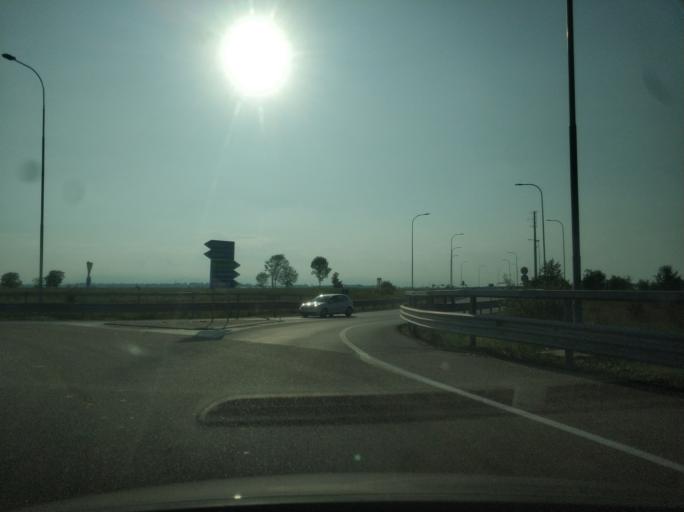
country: IT
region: Piedmont
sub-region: Provincia di Cuneo
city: Roreto
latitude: 44.6621
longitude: 7.8157
